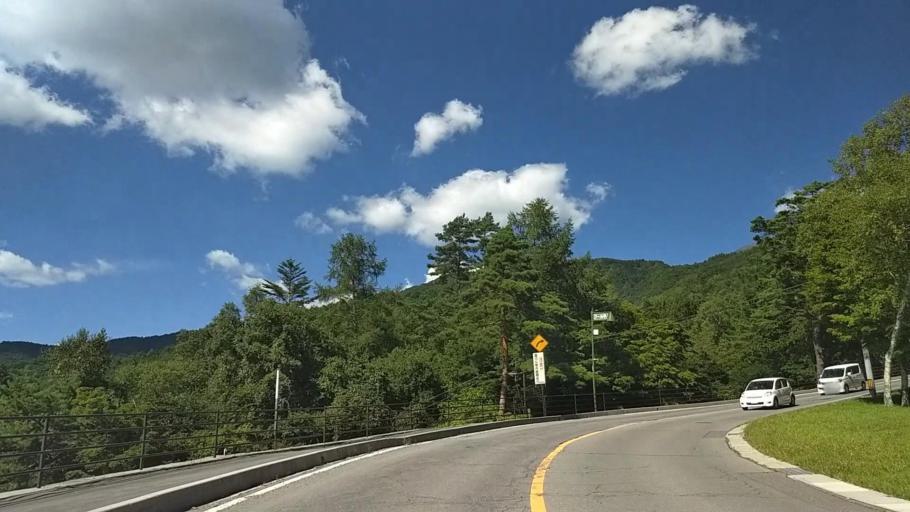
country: JP
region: Nagano
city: Chino
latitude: 36.0594
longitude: 138.2676
